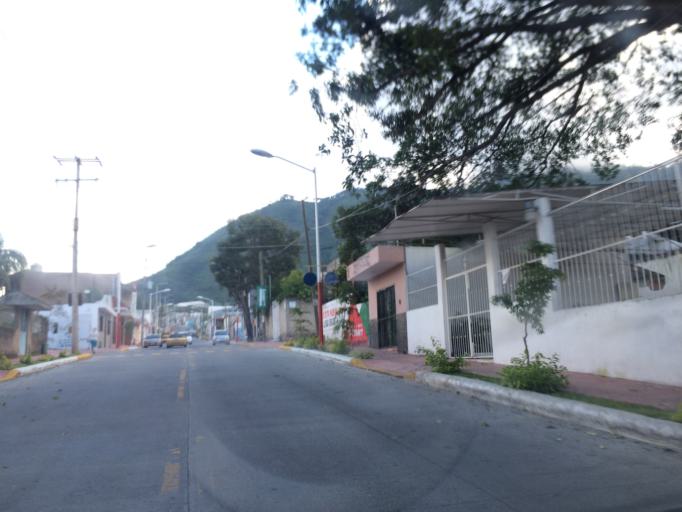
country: MX
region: Nayarit
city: Tepic
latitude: 21.4998
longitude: -104.9150
